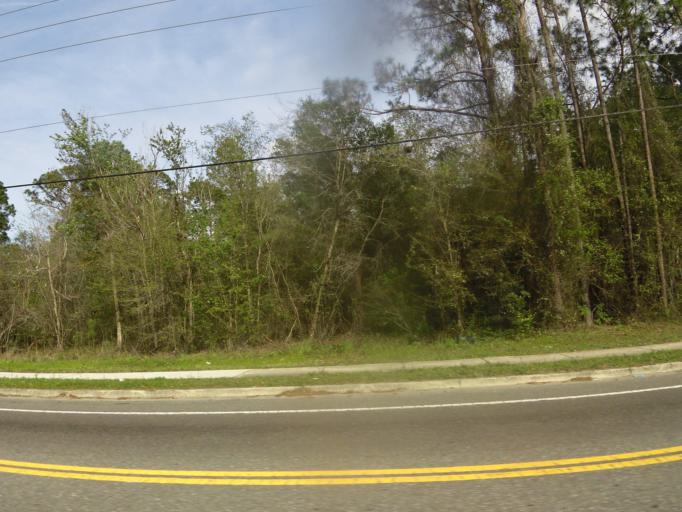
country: US
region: Florida
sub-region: Clay County
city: Bellair-Meadowbrook Terrace
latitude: 30.2556
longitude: -81.7860
